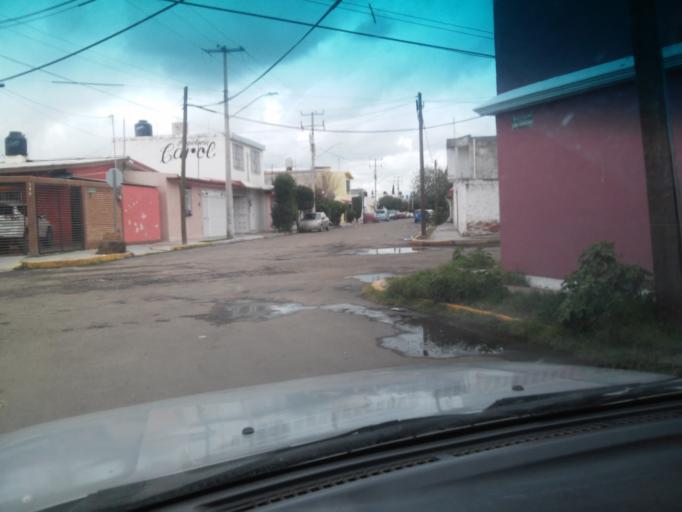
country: MX
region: Durango
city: Victoria de Durango
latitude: 24.0185
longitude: -104.6391
